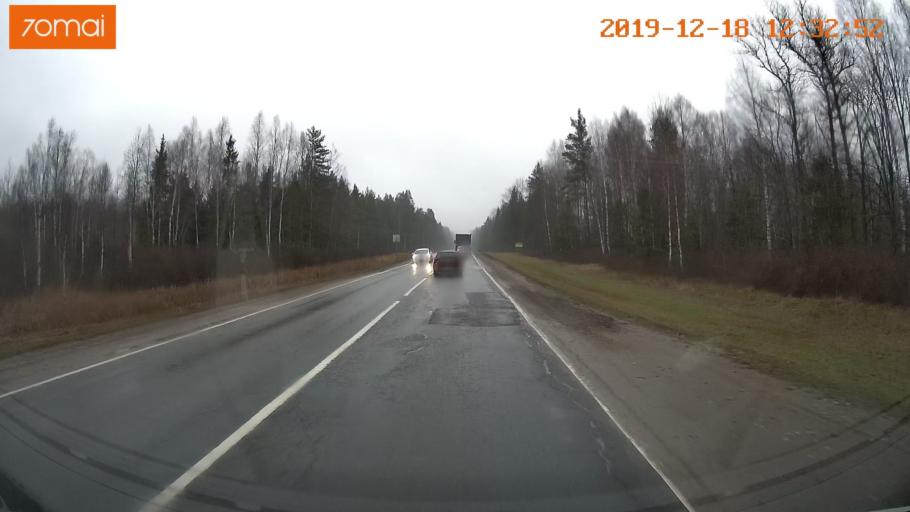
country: RU
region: Moskovskaya
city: Rumyantsevo
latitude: 56.1088
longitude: 36.5555
